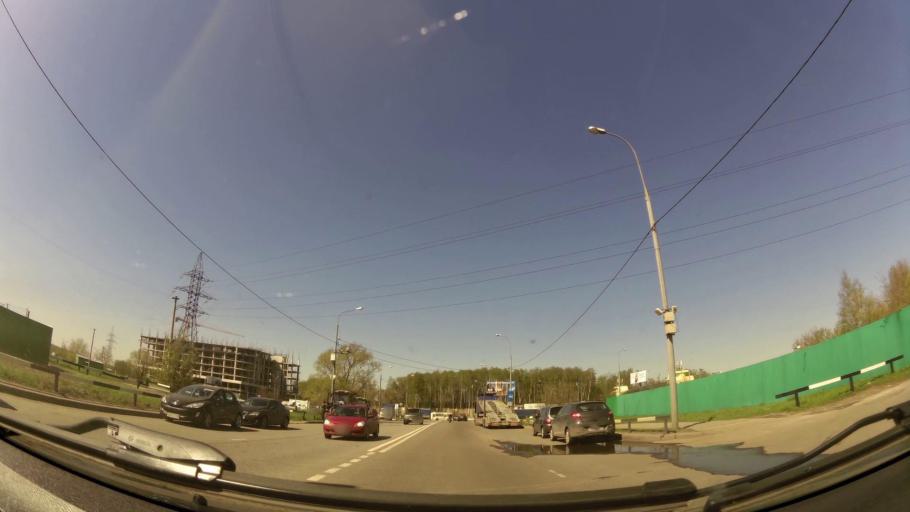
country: RU
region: Moscow
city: Strogino
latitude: 55.8013
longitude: 37.3868
